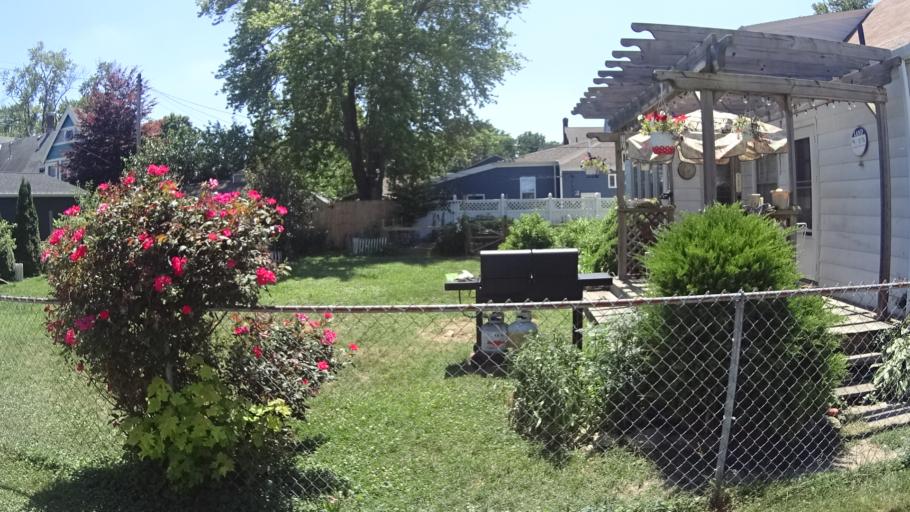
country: US
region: Ohio
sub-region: Erie County
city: Huron
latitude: 41.3936
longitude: -82.5596
